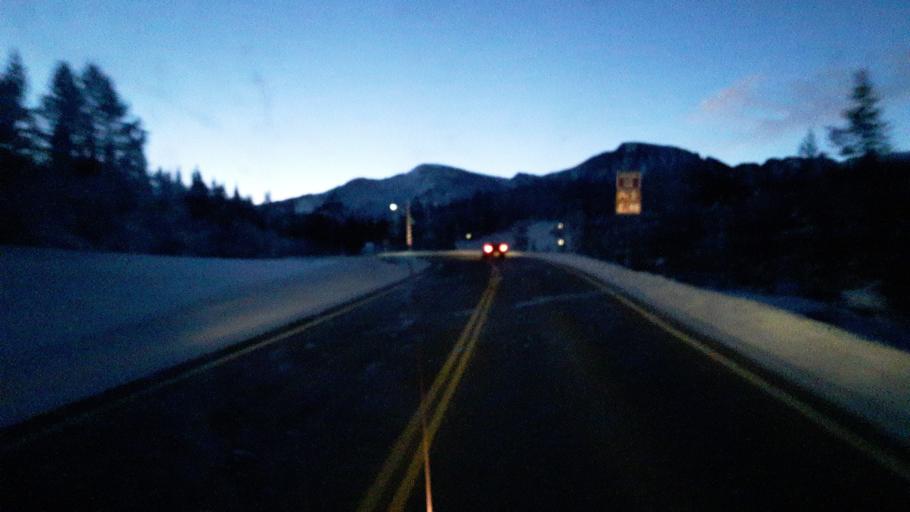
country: US
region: Colorado
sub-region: San Juan County
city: Silverton
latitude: 37.7344
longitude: -107.7125
